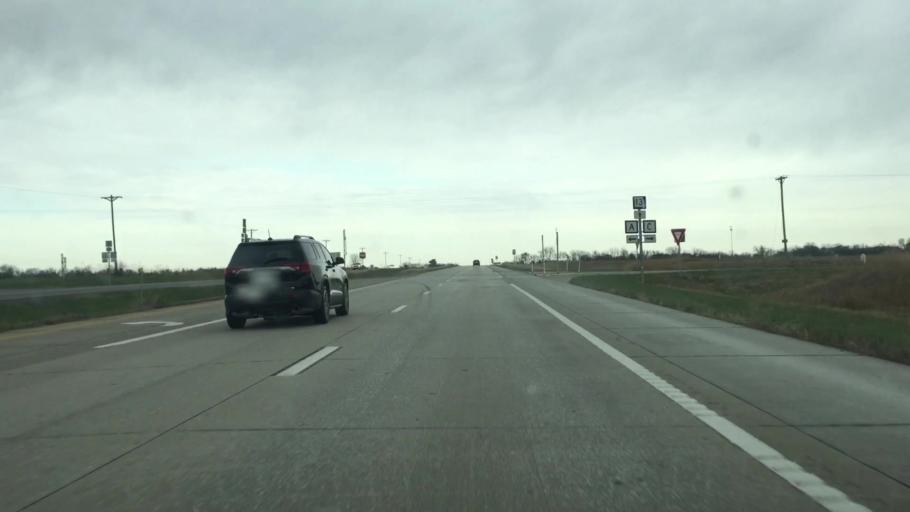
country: US
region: Missouri
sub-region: Saint Clair County
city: Osceola
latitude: 38.1511
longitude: -93.7227
